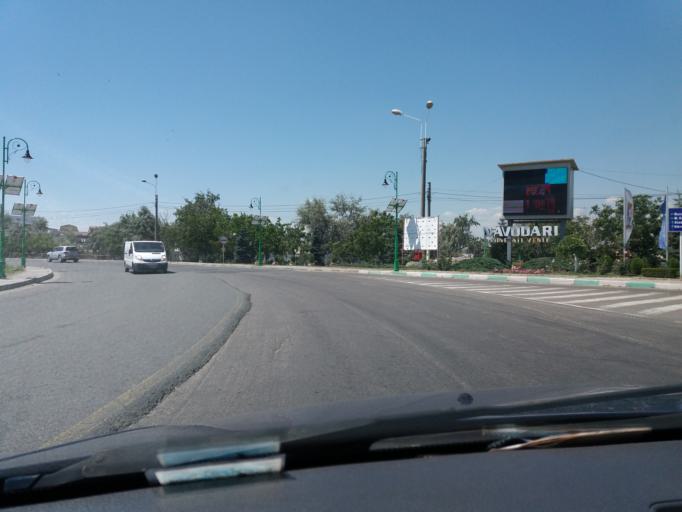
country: RO
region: Constanta
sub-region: Comuna Navodari
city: Navodari
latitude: 44.3228
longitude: 28.6185
